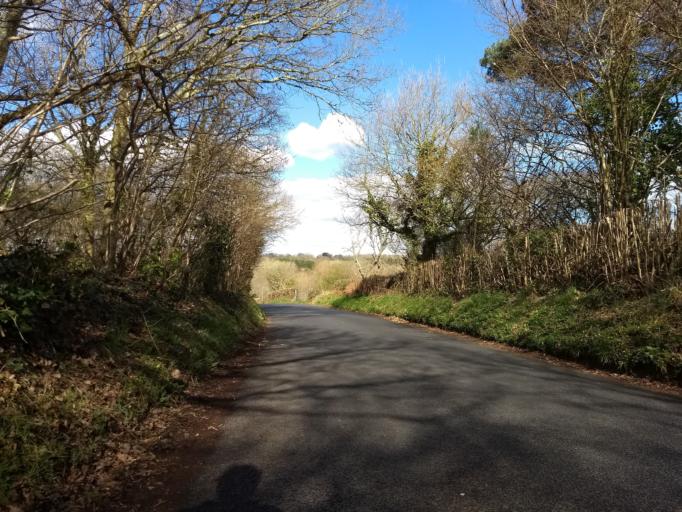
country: GB
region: England
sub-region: Isle of Wight
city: East Cowes
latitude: 50.7312
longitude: -1.2463
